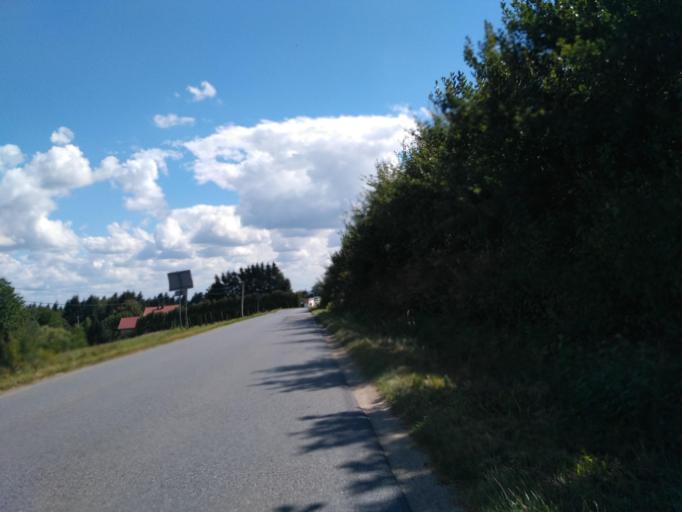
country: PL
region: Subcarpathian Voivodeship
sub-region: Powiat jasielski
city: Skolyszyn
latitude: 49.7853
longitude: 21.3451
